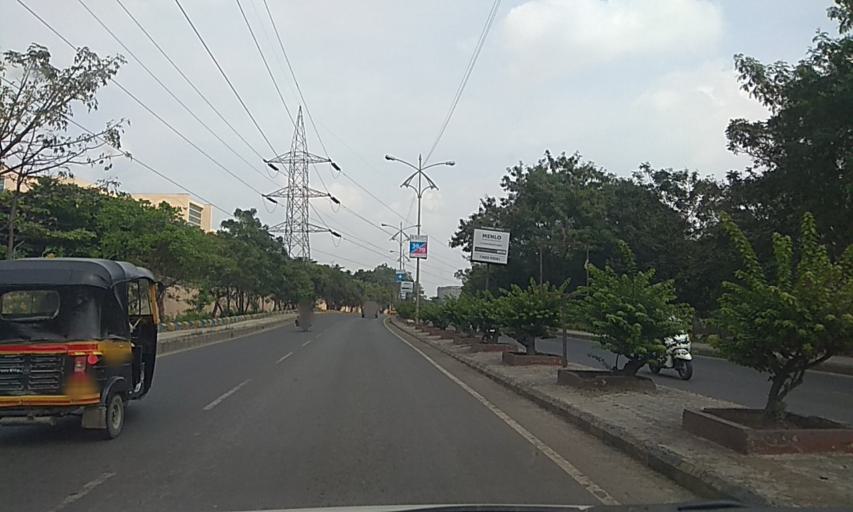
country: IN
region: Maharashtra
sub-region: Pune Division
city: Pimpri
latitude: 18.5953
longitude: 73.7113
